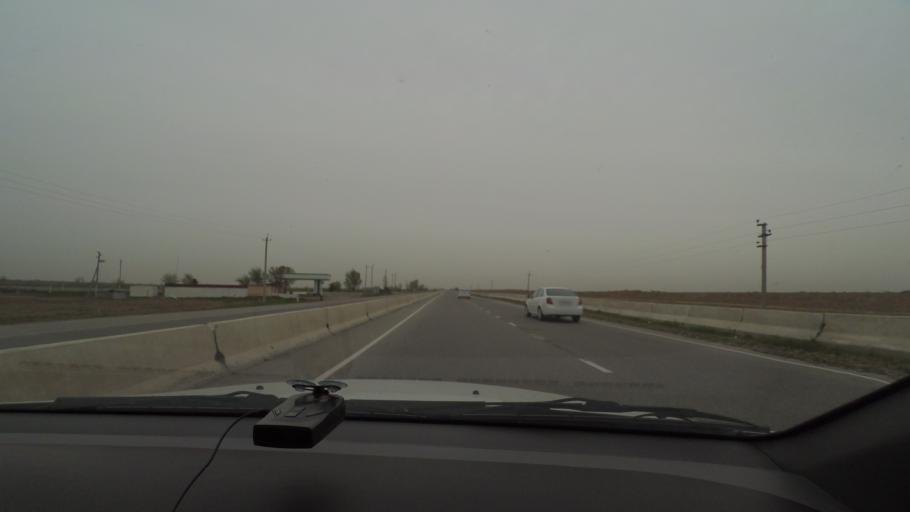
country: UZ
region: Jizzax
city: Gagarin
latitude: 40.4581
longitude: 68.2582
